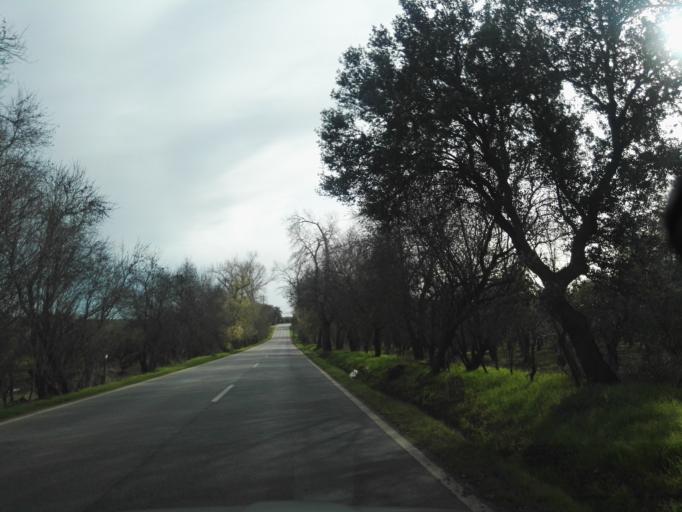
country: PT
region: Portalegre
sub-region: Elvas
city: Elvas
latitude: 38.9259
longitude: -7.1819
